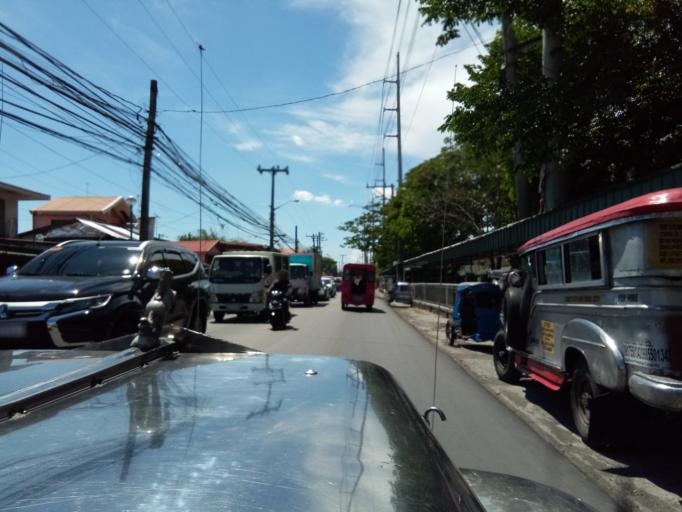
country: PH
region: Calabarzon
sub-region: Province of Cavite
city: General Trias
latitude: 14.3818
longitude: 120.8772
